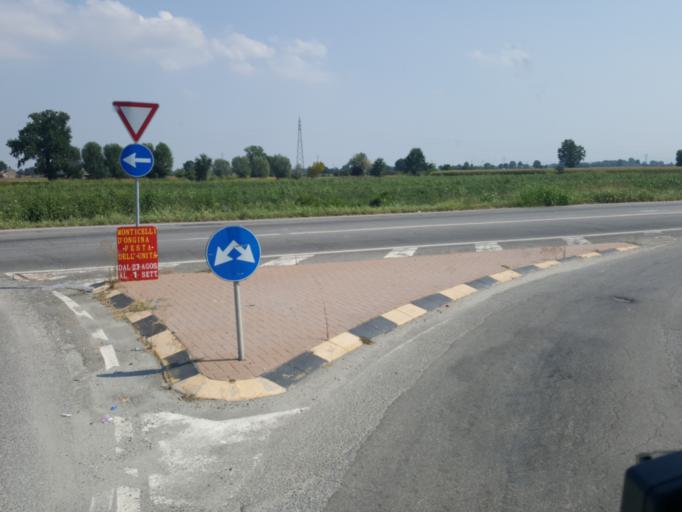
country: IT
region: Emilia-Romagna
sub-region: Provincia di Piacenza
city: Monticelli d'Ongina
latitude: 45.0785
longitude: 9.9061
